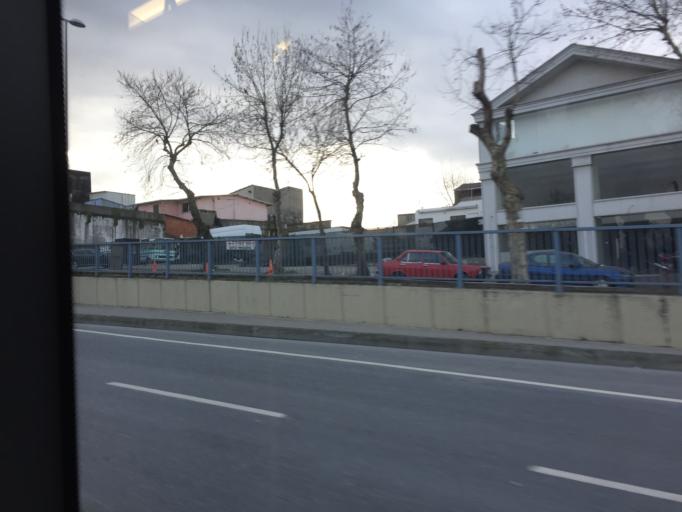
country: TR
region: Istanbul
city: Sisli
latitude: 41.0968
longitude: 29.0062
